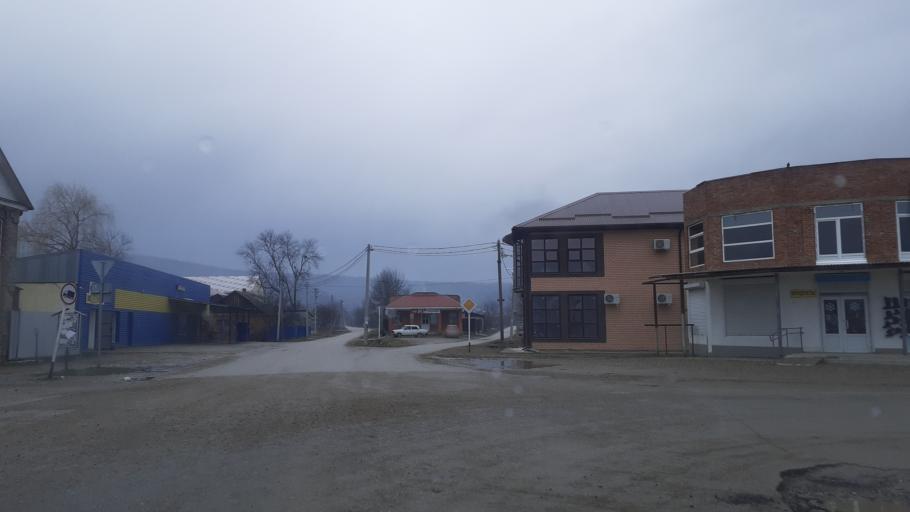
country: RU
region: Krasnodarskiy
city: Neftegorsk
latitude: 44.2476
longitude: 39.7658
